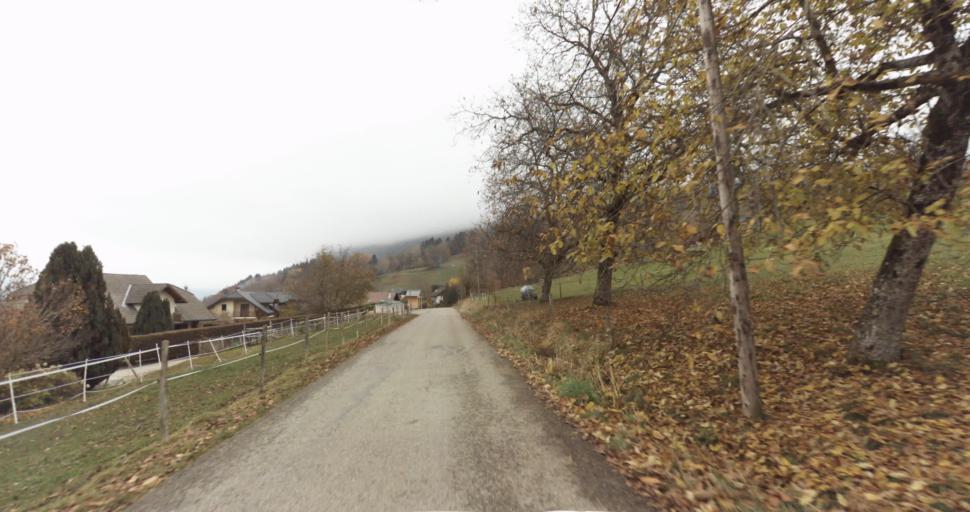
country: FR
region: Rhone-Alpes
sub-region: Departement de la Haute-Savoie
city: Saint-Jorioz
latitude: 45.8070
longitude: 6.1611
